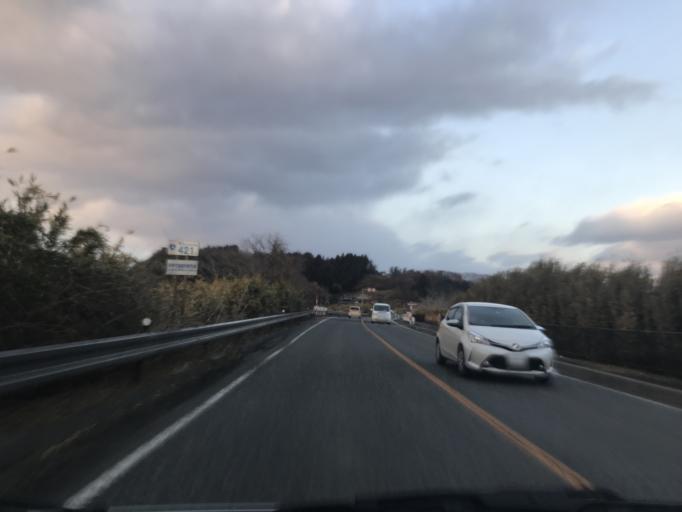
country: JP
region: Iwate
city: Ichinoseki
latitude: 38.7766
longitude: 141.0437
